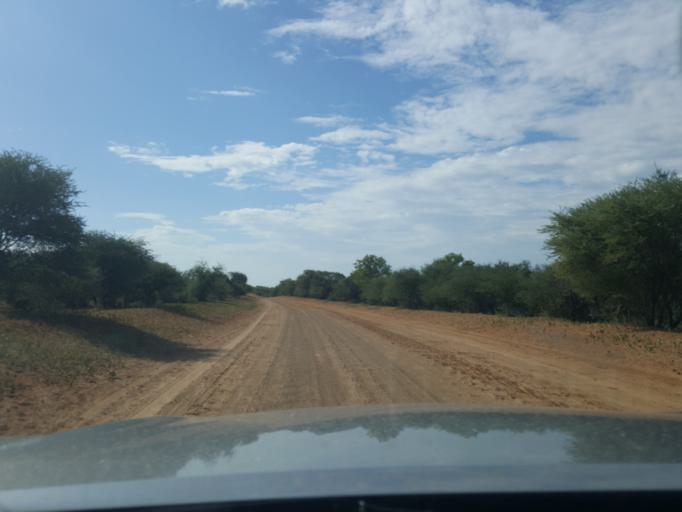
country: BW
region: Kweneng
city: Khudumelapye
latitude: -23.5396
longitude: 24.7287
